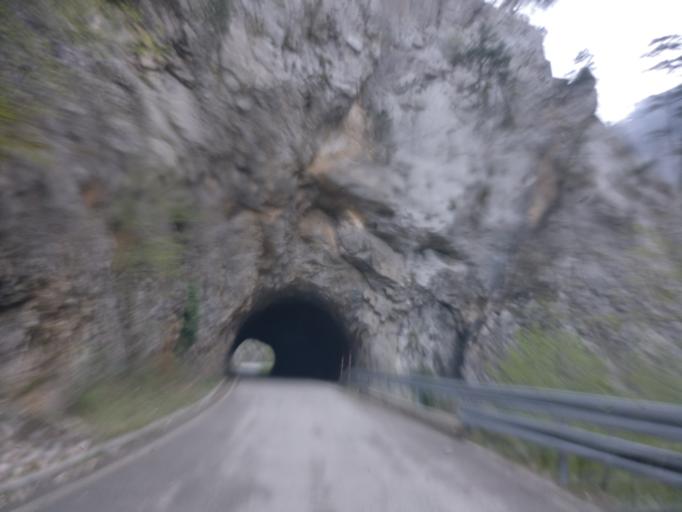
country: ME
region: Opstina Pluzine
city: Pluzine
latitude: 43.2809
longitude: 18.8496
